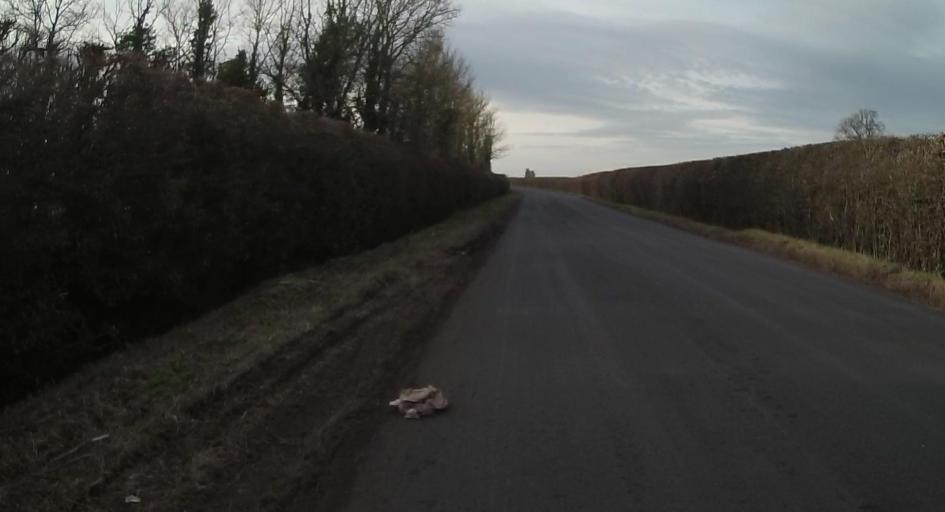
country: GB
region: England
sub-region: West Berkshire
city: Stratfield Mortimer
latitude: 51.4044
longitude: -1.0334
